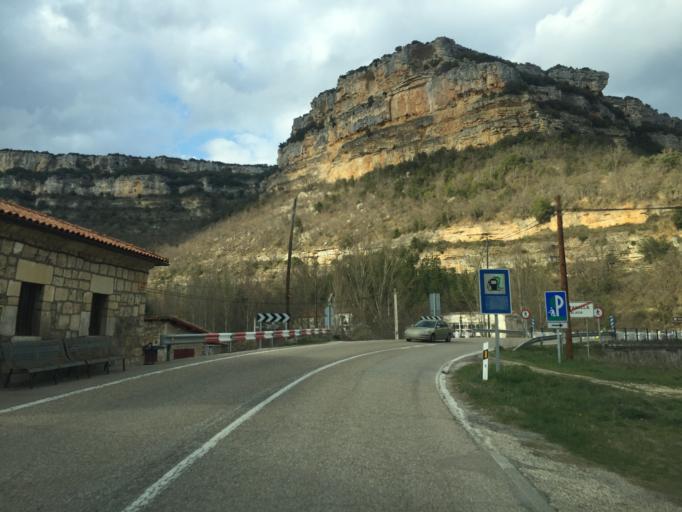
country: ES
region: Castille and Leon
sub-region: Provincia de Burgos
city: Tubilla del Agua
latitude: 42.8006
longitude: -3.7697
